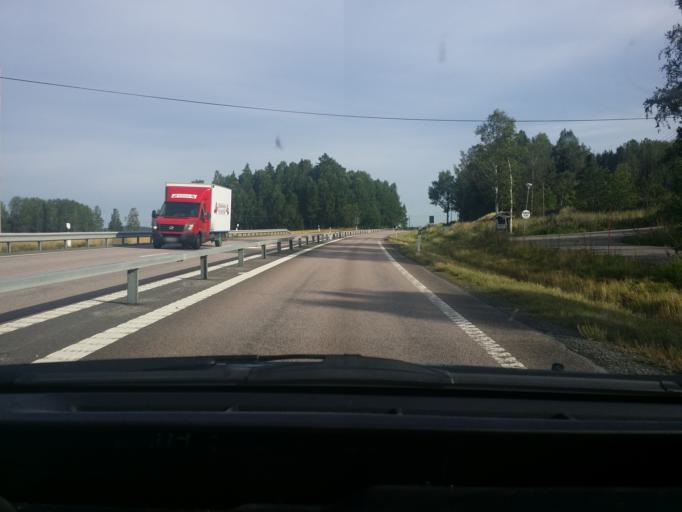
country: SE
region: Vaestmanland
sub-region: Vasteras
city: Hokasen
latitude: 59.7287
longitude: 16.5657
